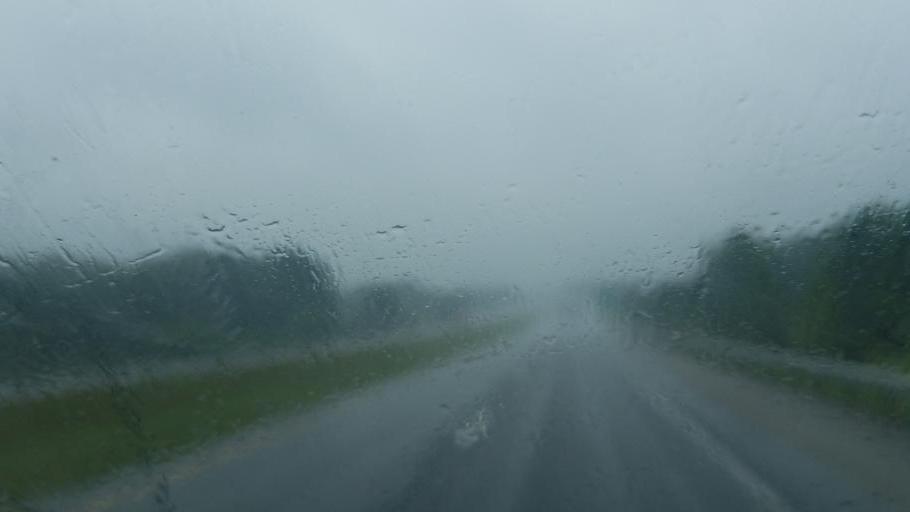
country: US
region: Indiana
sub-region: Delaware County
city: Yorktown
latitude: 40.2255
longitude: -85.5594
